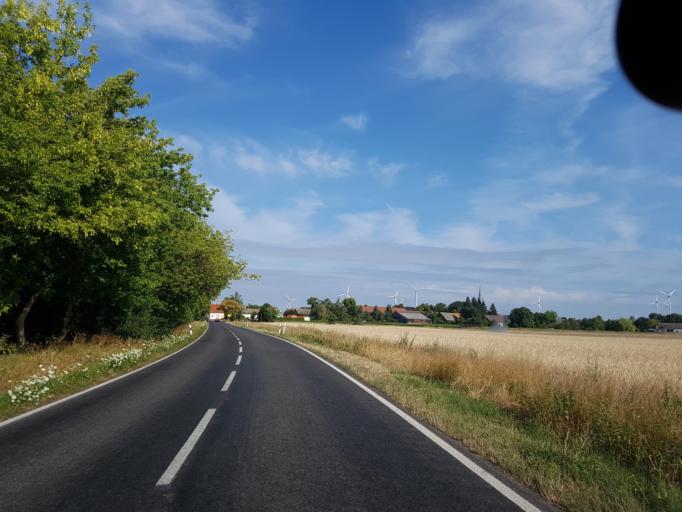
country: DE
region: Brandenburg
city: Ihlow
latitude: 51.9503
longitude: 13.3301
